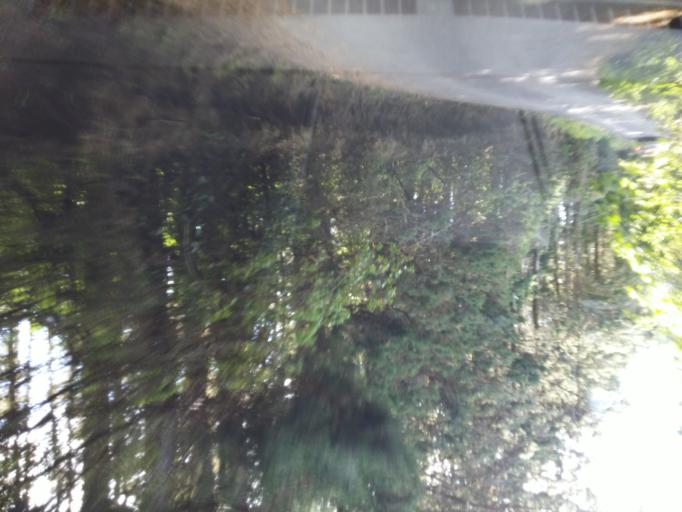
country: CR
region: Heredia
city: Santo Domingo
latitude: 10.1124
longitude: -84.1236
